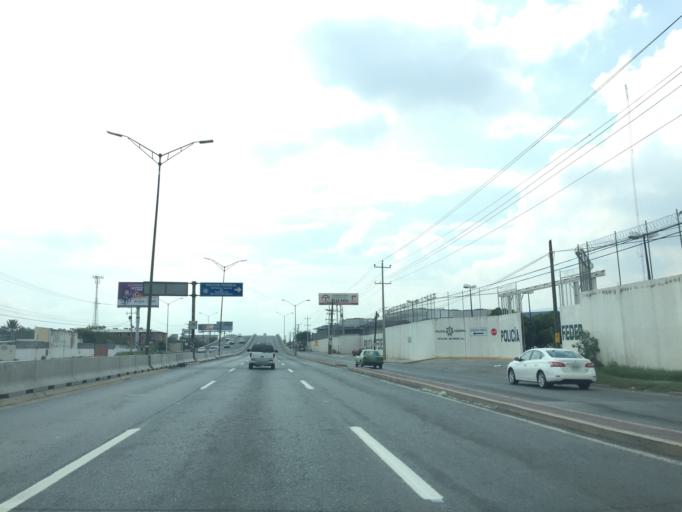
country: MX
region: Nuevo Leon
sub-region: Apodaca
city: Fraccionamiento Cosmopolis Octavo Sector
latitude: 25.8064
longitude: -100.2747
